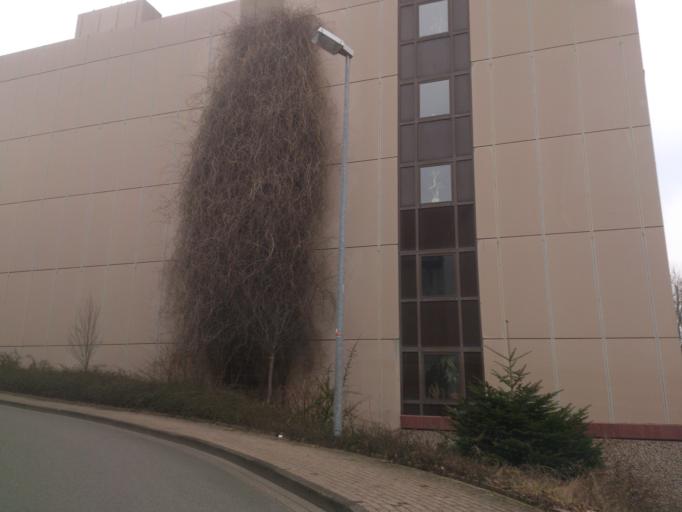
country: DE
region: North Rhine-Westphalia
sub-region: Regierungsbezirk Detmold
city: Vlotho
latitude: 52.1696
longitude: 8.8643
